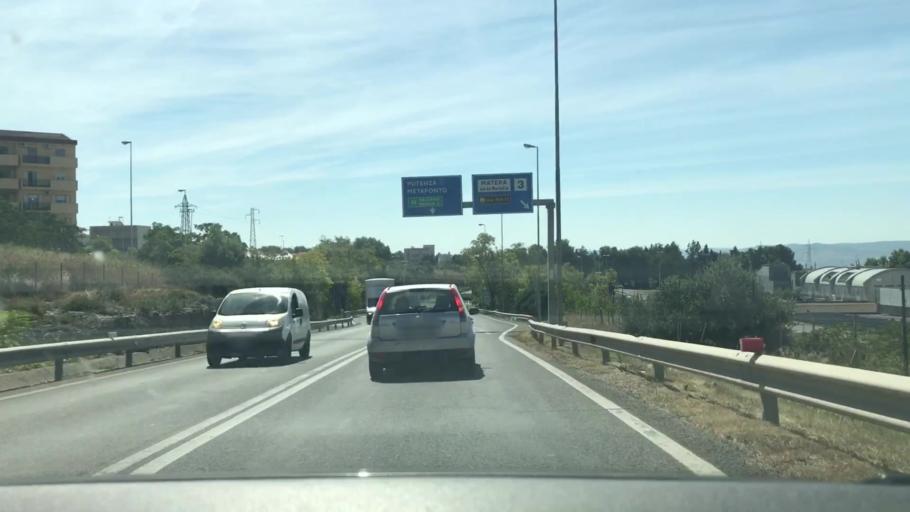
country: IT
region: Basilicate
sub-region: Provincia di Matera
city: Matera
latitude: 40.6722
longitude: 16.5777
